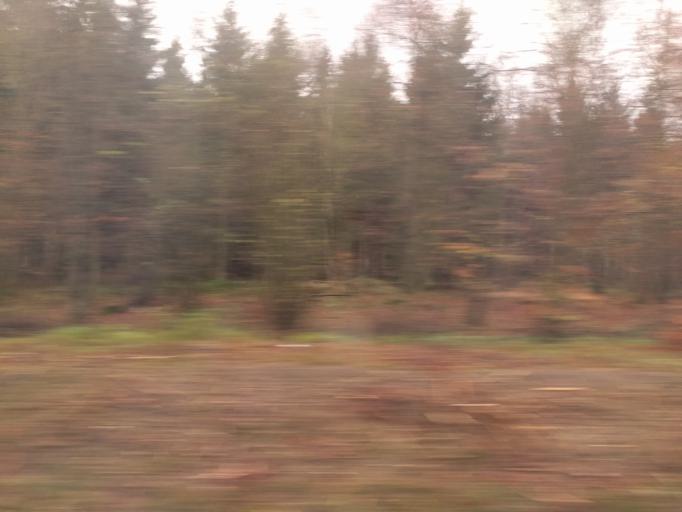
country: DK
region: Zealand
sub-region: Koge Kommune
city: Borup
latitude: 55.5055
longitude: 11.9742
